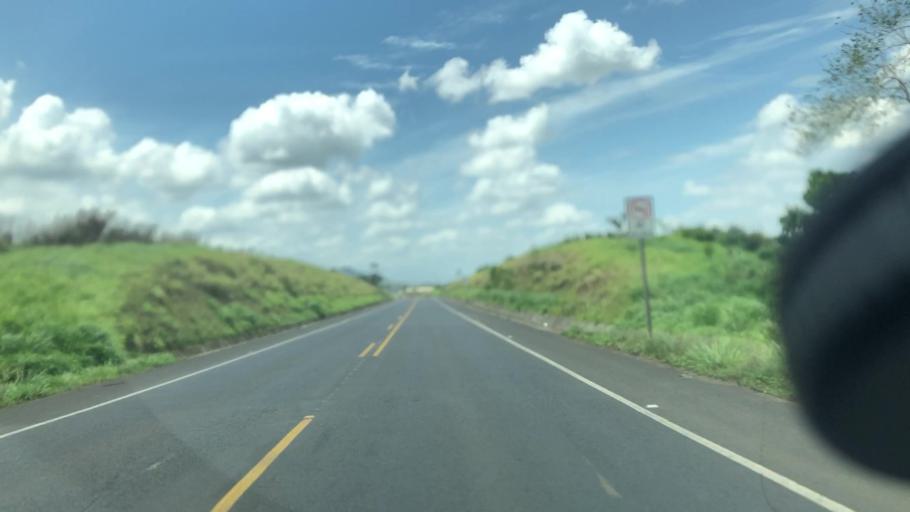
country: CR
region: Alajuela
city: Pital
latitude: 10.4346
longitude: -84.2860
